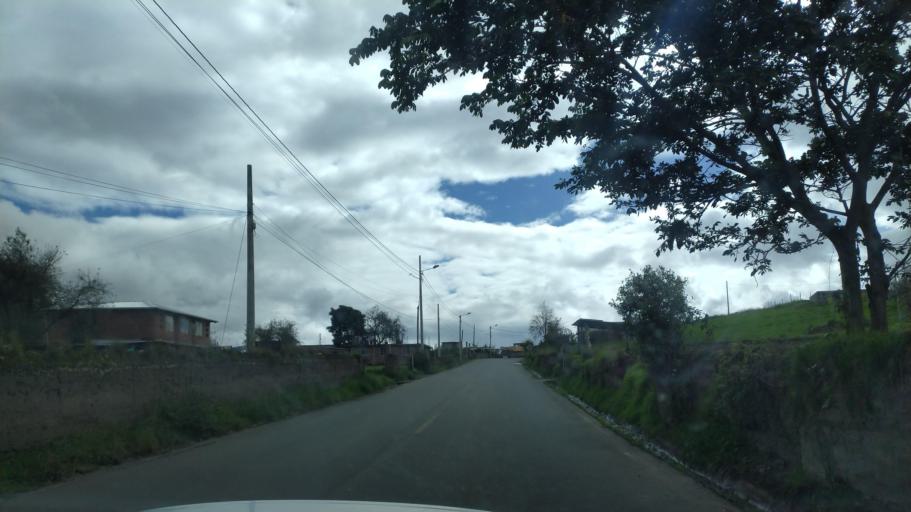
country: EC
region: Chimborazo
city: Riobamba
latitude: -1.6612
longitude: -78.5785
